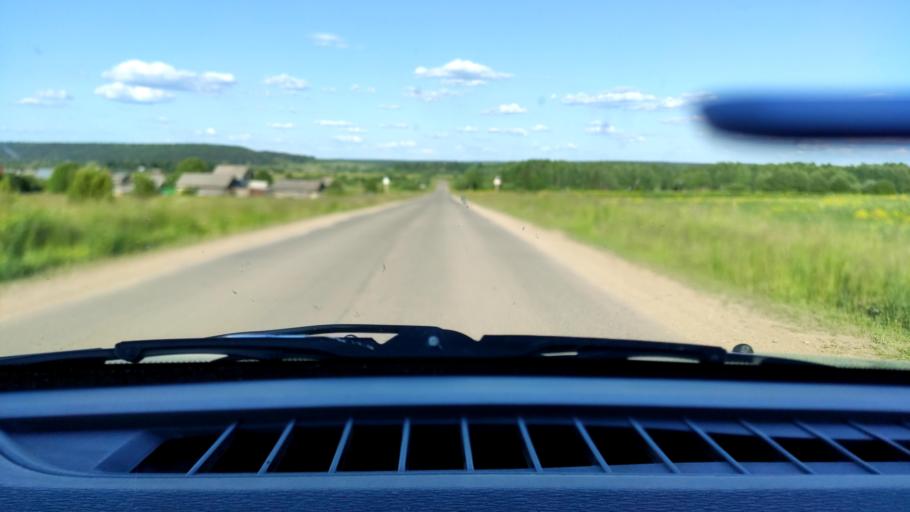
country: RU
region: Perm
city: Uinskoye
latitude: 57.0708
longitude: 56.5740
